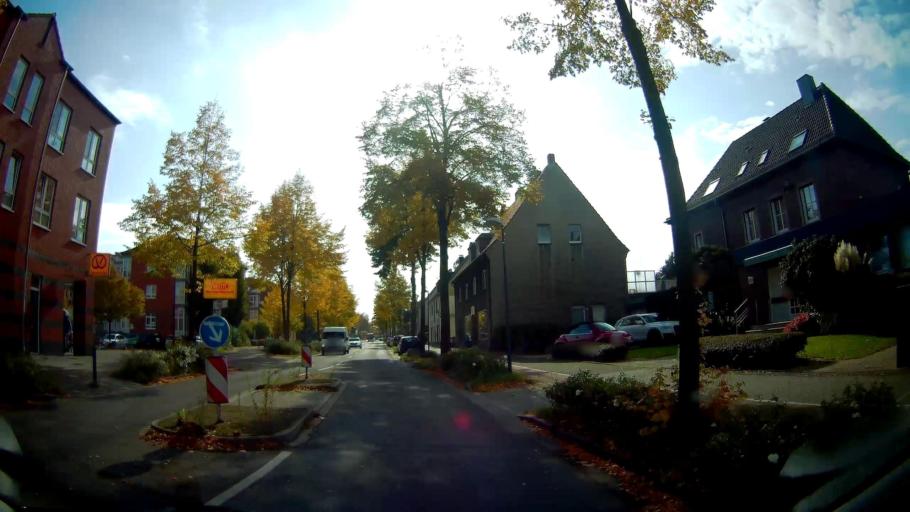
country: DE
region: North Rhine-Westphalia
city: Herten
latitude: 51.6186
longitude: 7.1421
